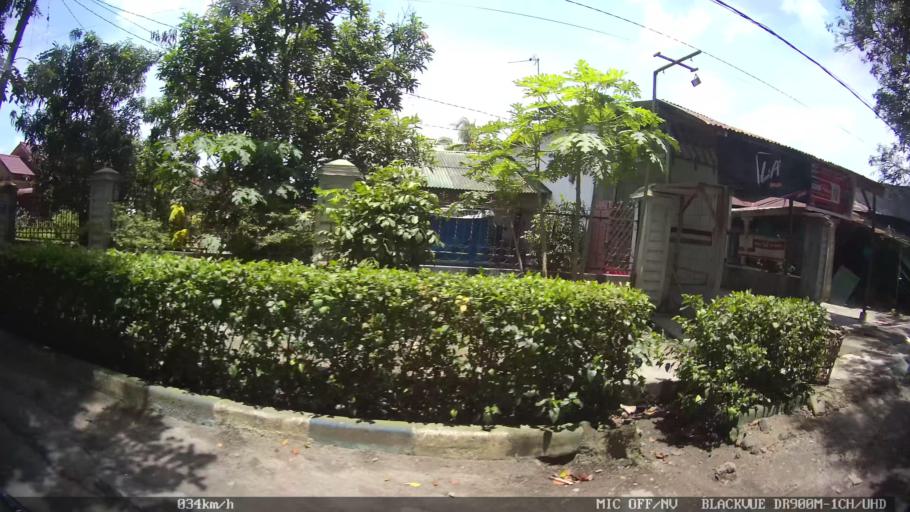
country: ID
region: North Sumatra
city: Percut
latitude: 3.5574
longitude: 98.8574
